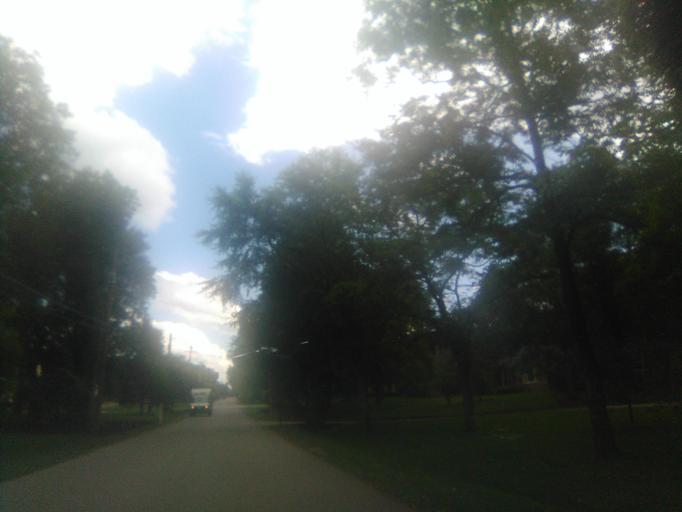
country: US
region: Tennessee
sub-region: Davidson County
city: Belle Meade
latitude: 36.0992
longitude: -86.8344
